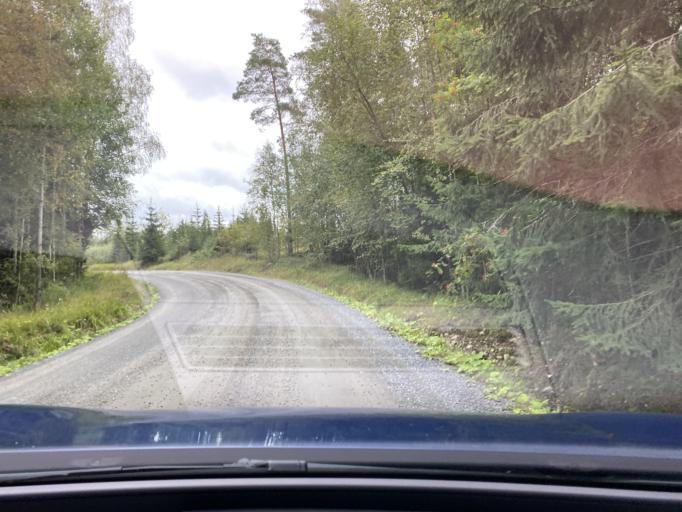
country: FI
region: Pirkanmaa
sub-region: Lounais-Pirkanmaa
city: Vammala
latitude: 61.2657
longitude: 22.9889
